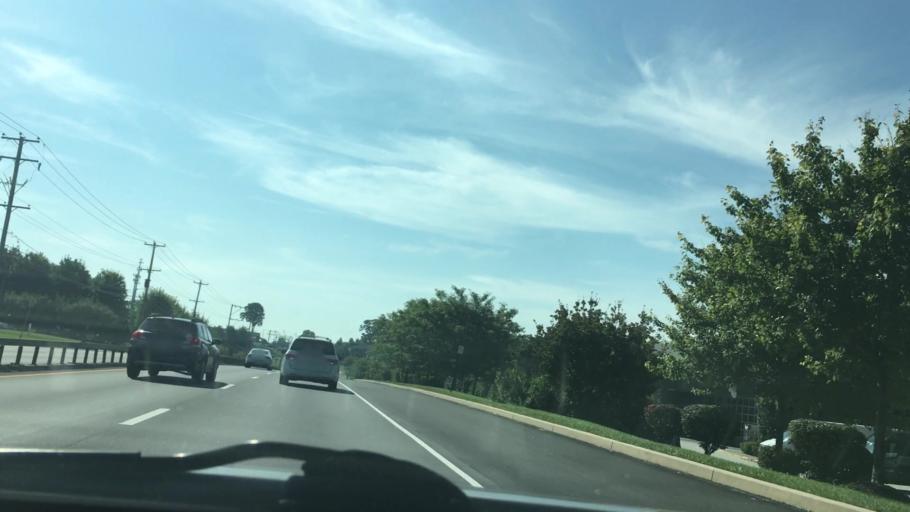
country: US
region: Pennsylvania
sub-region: Chester County
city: West Chester
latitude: 39.9104
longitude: -75.5705
